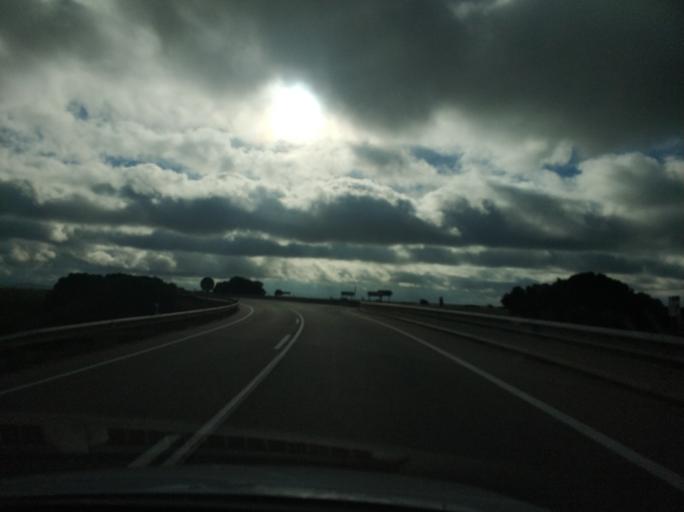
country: ES
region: Castille and Leon
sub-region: Provincia de Soria
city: Fuentecambron
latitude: 41.4968
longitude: -3.3100
